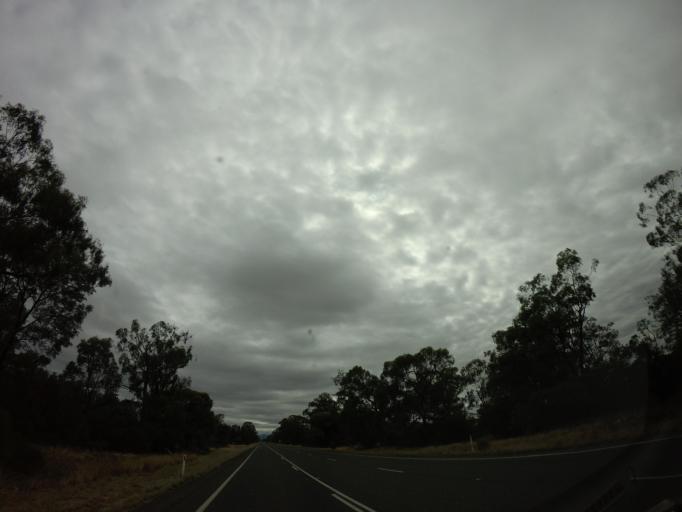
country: AU
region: New South Wales
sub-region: Narrabri
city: Narrabri
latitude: -30.3535
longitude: 149.7489
